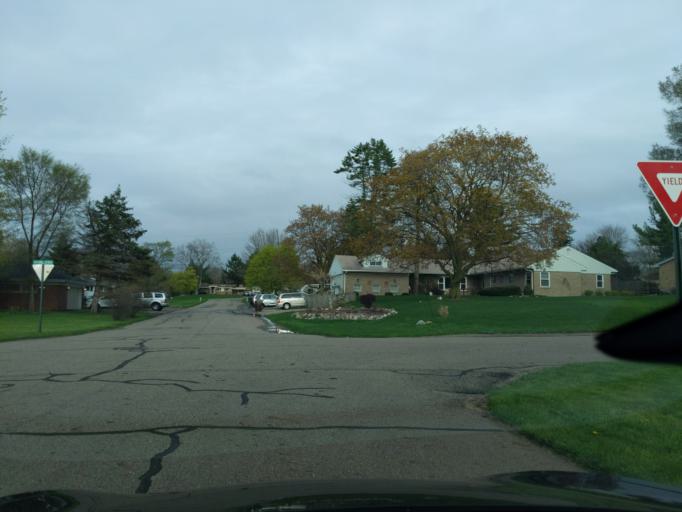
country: US
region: Michigan
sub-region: Eaton County
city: Waverly
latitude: 42.7301
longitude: -84.6105
